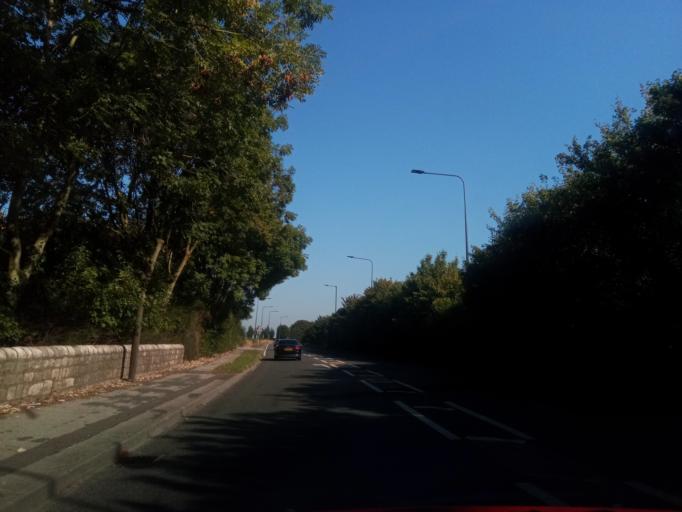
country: GB
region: England
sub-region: Doncaster
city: Conisbrough
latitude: 53.4931
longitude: -1.1924
